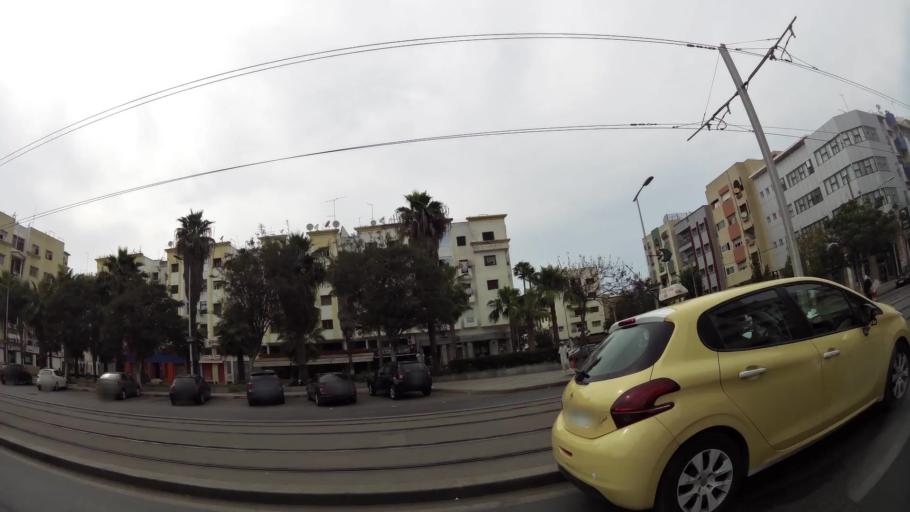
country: MA
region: Rabat-Sale-Zemmour-Zaer
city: Sale
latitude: 34.0445
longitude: -6.8085
